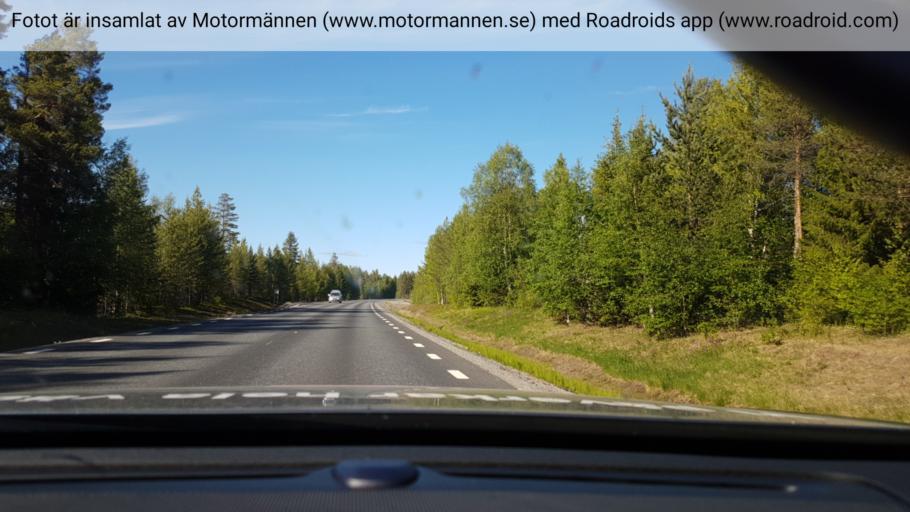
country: SE
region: Vaesterbotten
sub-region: Lycksele Kommun
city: Lycksele
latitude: 64.8045
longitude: 18.7328
